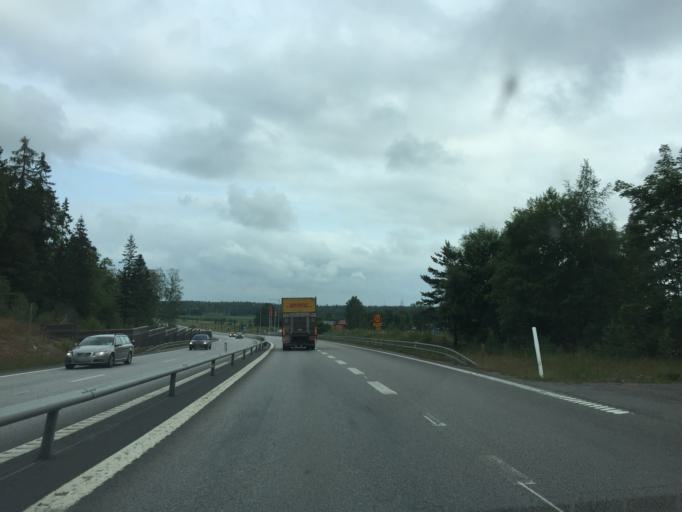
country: SE
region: OErebro
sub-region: Lekebergs Kommun
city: Fjugesta
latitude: 59.2535
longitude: 14.8210
